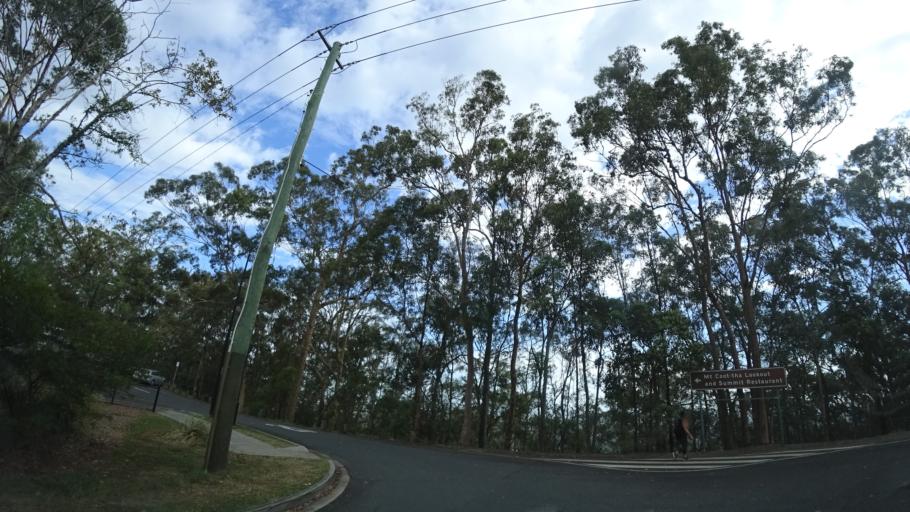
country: AU
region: Queensland
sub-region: Brisbane
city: Taringa
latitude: -27.4846
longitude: 152.9573
